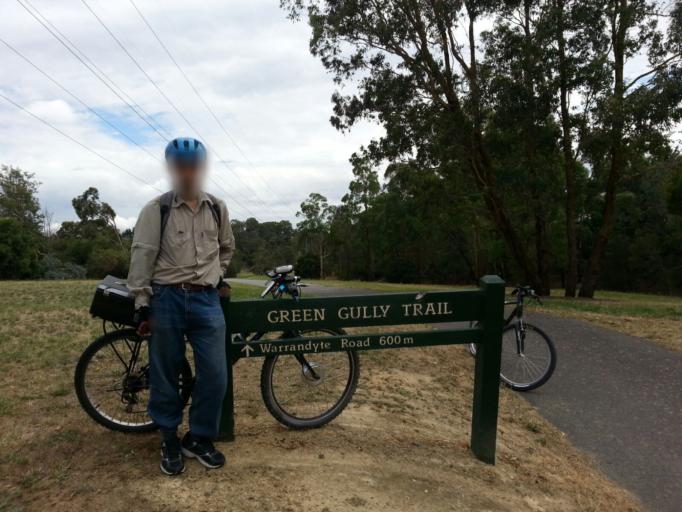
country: AU
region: Victoria
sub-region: Nillumbik
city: Eltham
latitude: -37.7557
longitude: 145.1636
